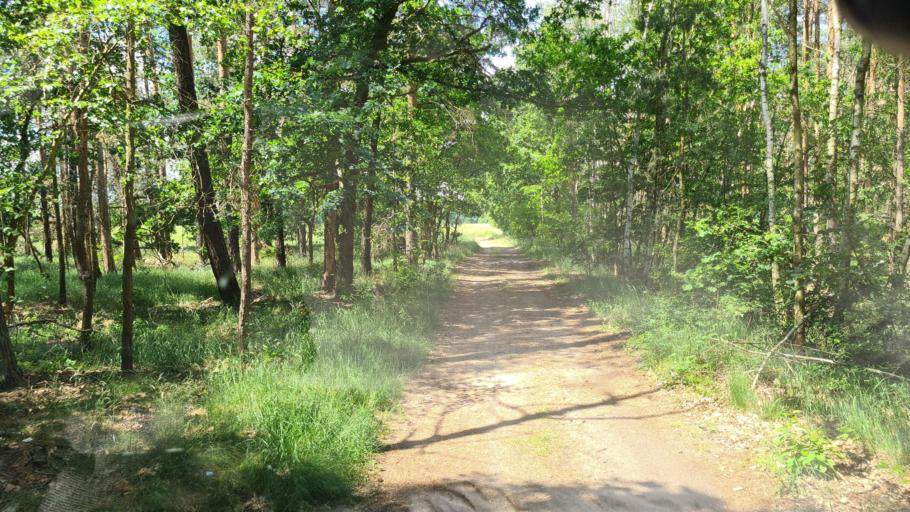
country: DE
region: Brandenburg
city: Sallgast
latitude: 51.5918
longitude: 13.8235
